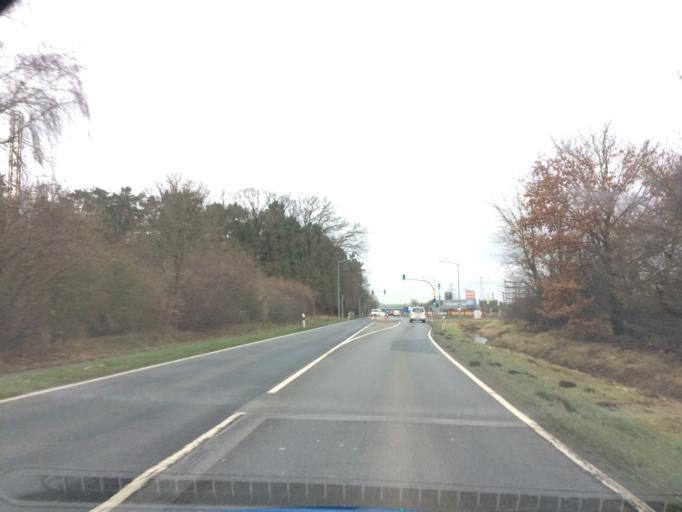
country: DE
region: Lower Saxony
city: Winsen
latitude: 53.3324
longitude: 10.2147
